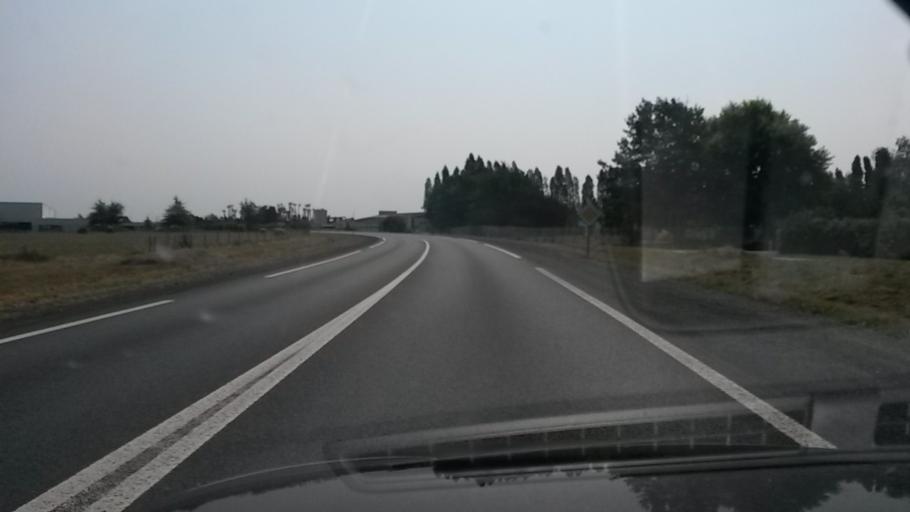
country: FR
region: Pays de la Loire
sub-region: Departement de la Loire-Atlantique
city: Mesanger
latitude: 47.4146
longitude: -1.1893
